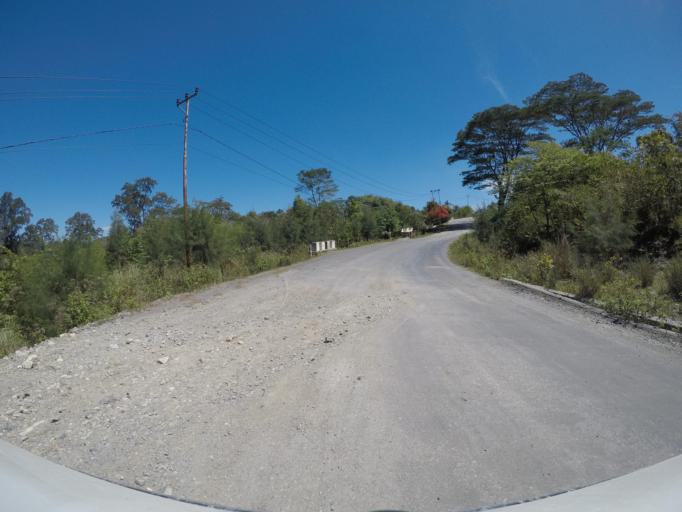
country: TL
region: Manatuto
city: Manatuto
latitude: -8.7929
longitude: 125.9702
